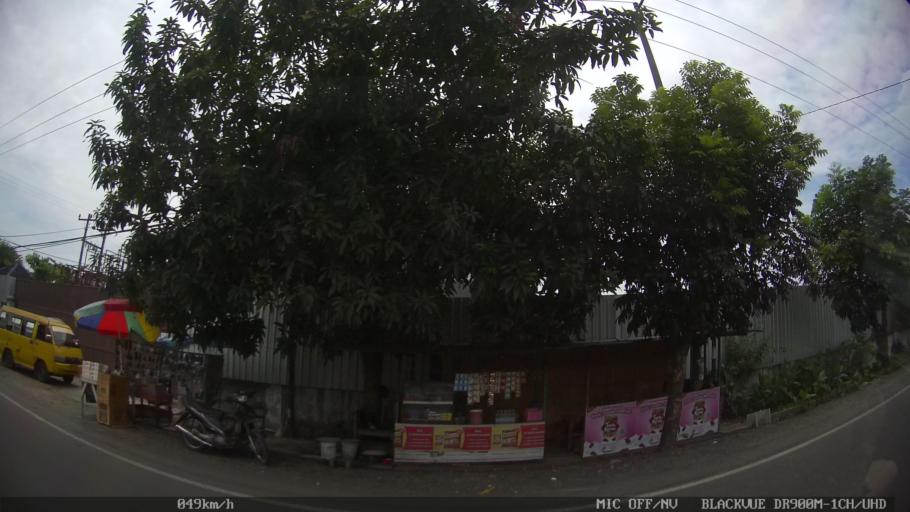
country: ID
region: North Sumatra
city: Sunggal
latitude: 3.5996
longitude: 98.5828
